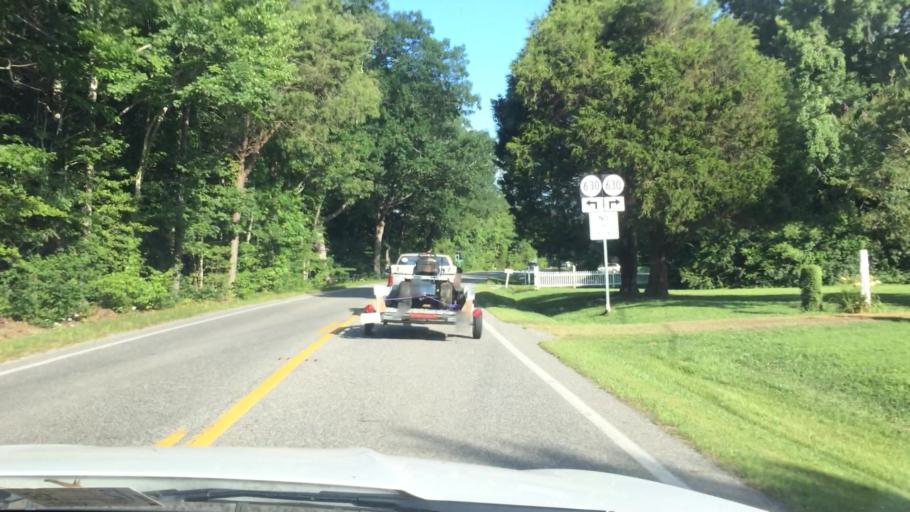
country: US
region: Virginia
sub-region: Middlesex County
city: Deltaville
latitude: 37.5393
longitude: -76.4310
